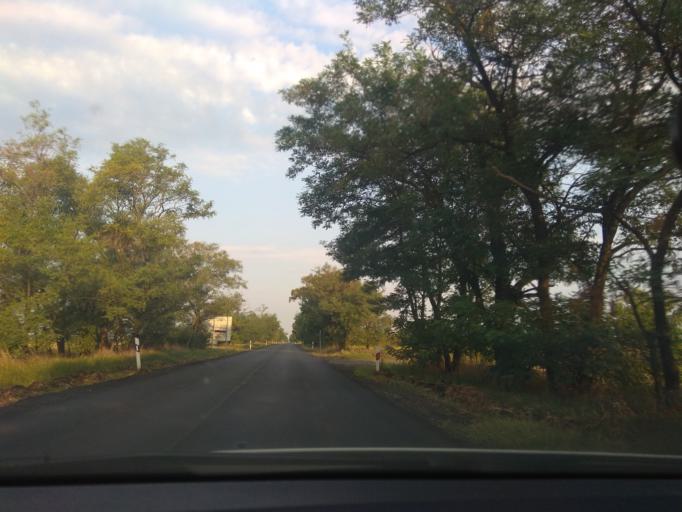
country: HU
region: Borsod-Abauj-Zemplen
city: Mezokovesd
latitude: 47.8112
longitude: 20.5394
